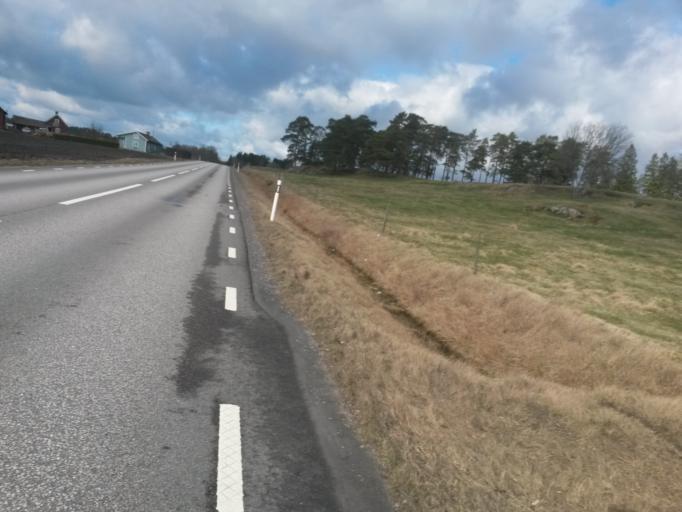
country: SE
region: Vaestra Goetaland
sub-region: Vargarda Kommun
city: Vargarda
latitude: 58.0516
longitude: 12.7717
